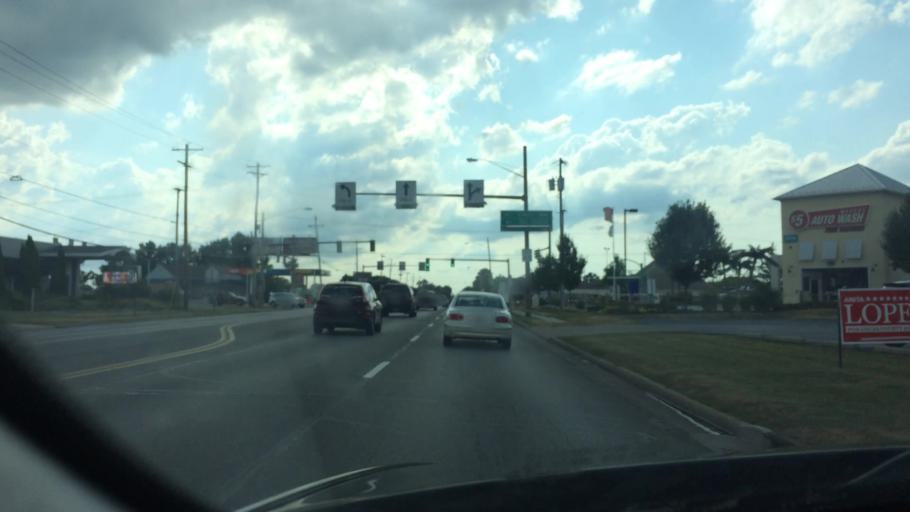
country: US
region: Ohio
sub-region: Lucas County
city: Maumee
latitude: 41.5944
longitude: -83.6443
